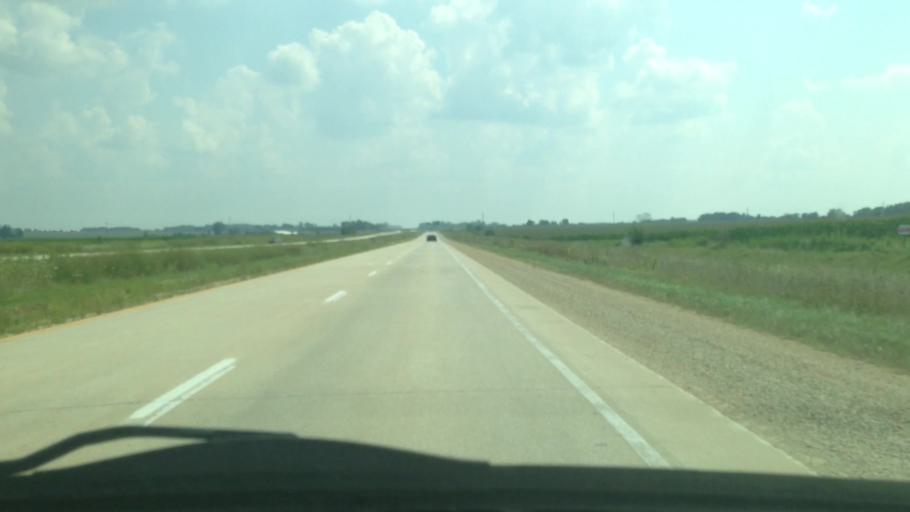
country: US
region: Iowa
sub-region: Chickasaw County
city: New Hampton
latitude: 42.9785
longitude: -92.3178
